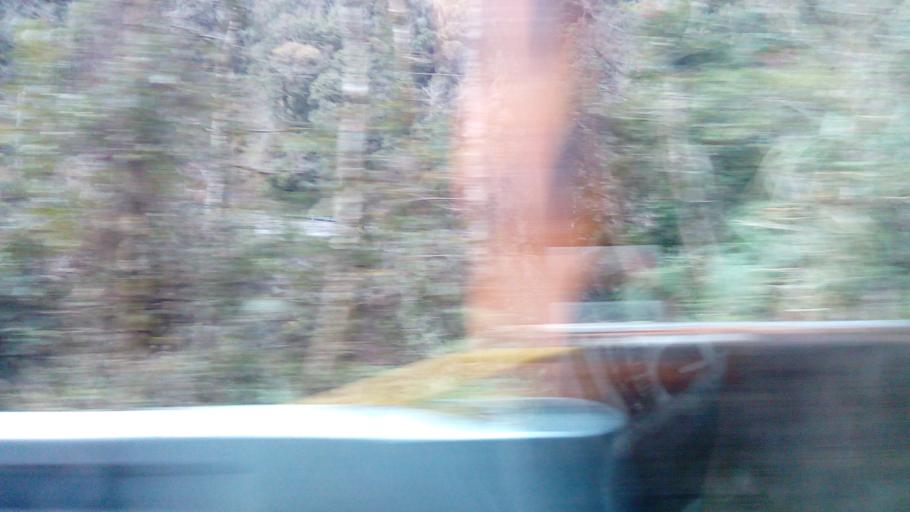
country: TW
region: Taiwan
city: Daxi
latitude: 24.4042
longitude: 121.3620
